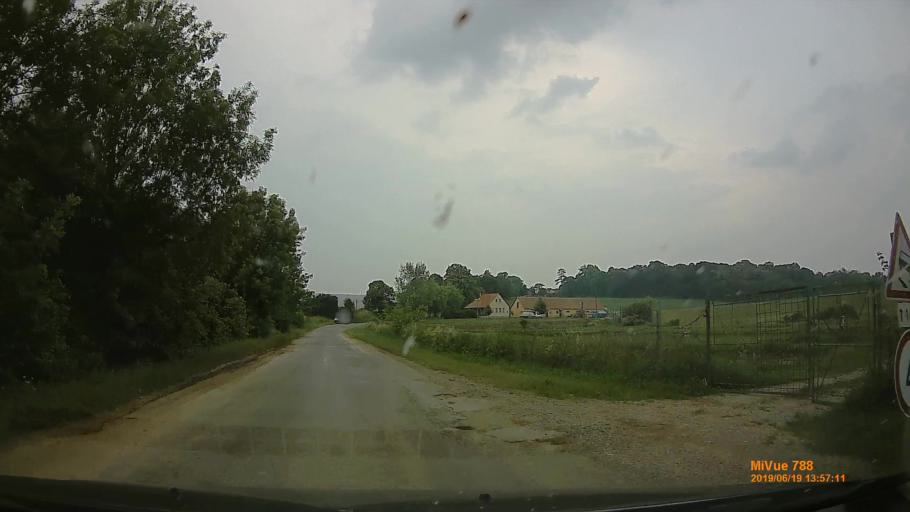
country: HU
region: Baranya
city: Szigetvar
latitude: 46.0838
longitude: 17.8034
